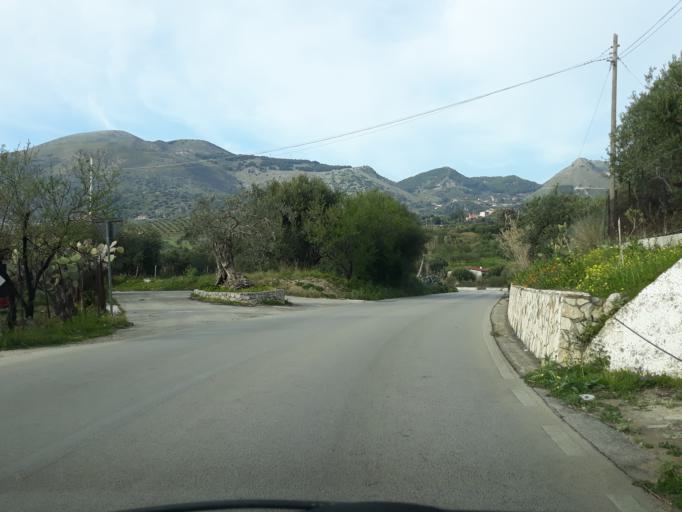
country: IT
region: Sicily
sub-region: Palermo
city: Giardinello
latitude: 38.0698
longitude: 13.1540
